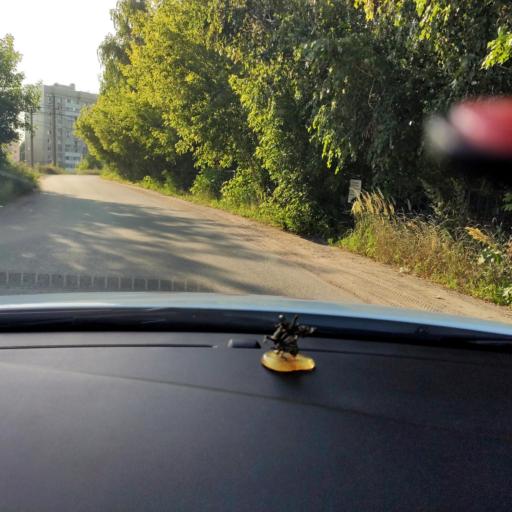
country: RU
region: Tatarstan
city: Staroye Arakchino
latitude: 55.8127
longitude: 48.9129
